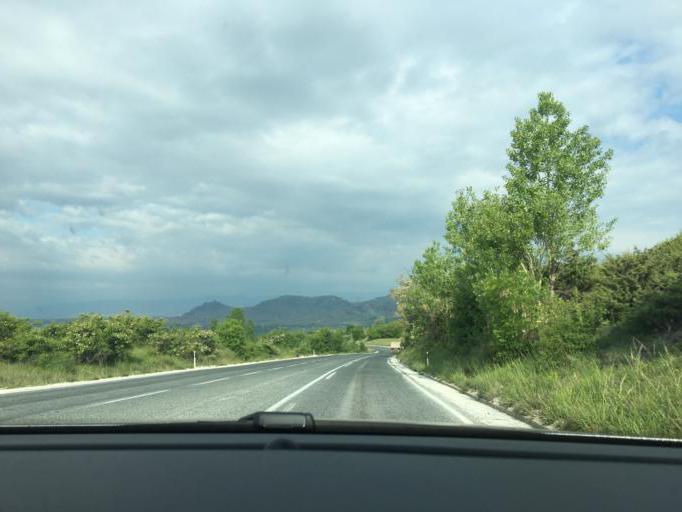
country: MK
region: Prilep
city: Prilep
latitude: 41.3689
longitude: 21.6359
